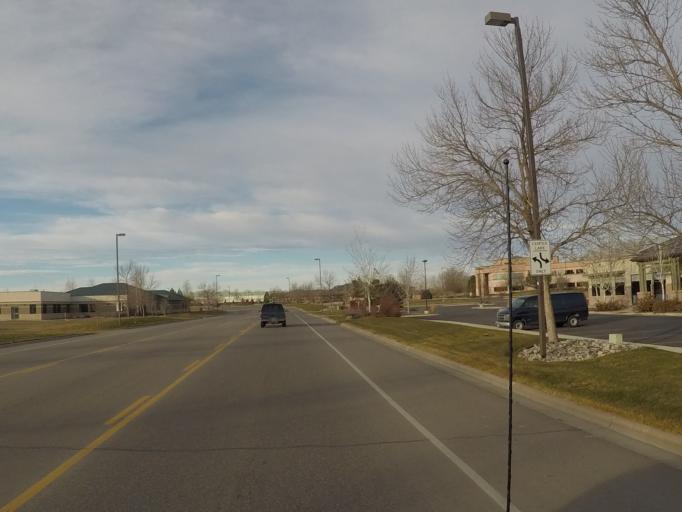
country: US
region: Montana
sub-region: Yellowstone County
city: Billings
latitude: 45.7443
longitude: -108.6012
